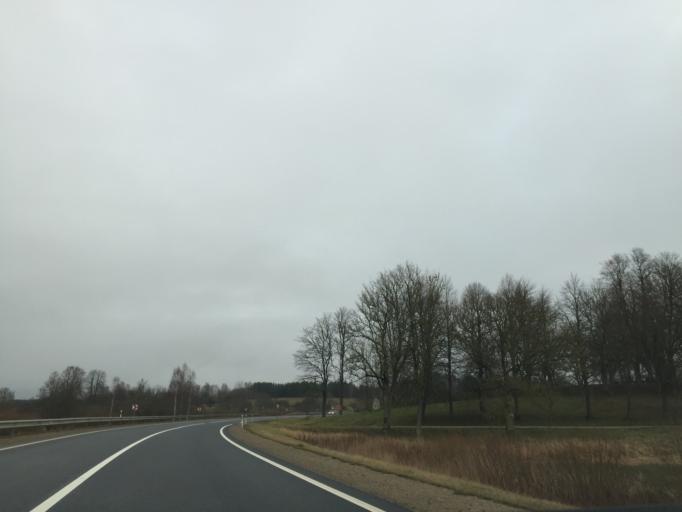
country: LV
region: Durbe
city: Liegi
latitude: 56.5902
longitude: 21.3616
